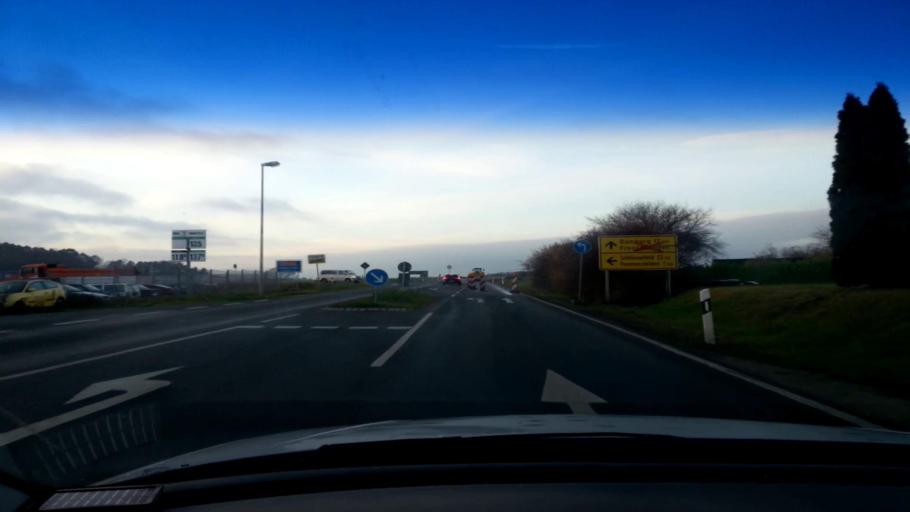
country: DE
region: Bavaria
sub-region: Upper Franconia
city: Frensdorf
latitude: 49.7944
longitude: 10.8834
